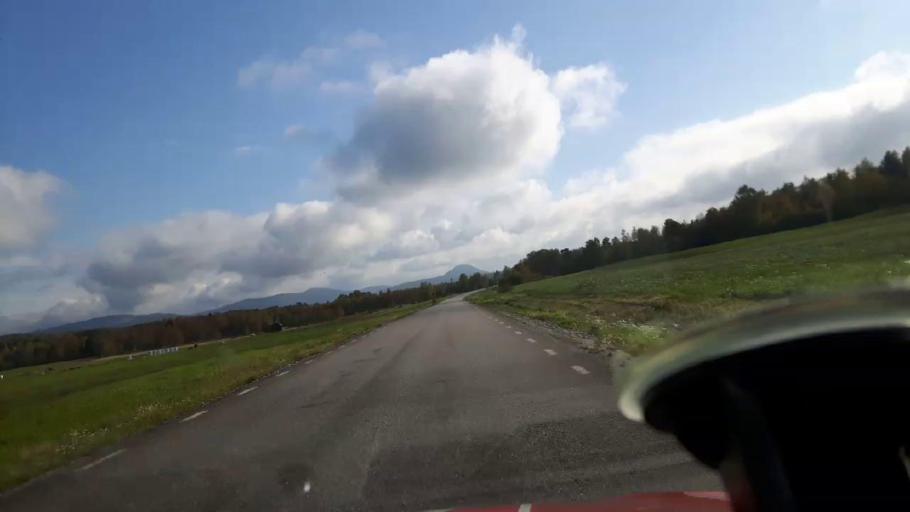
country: SE
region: Gaevleborg
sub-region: Ljusdals Kommun
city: Ljusdal
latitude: 61.7607
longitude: 16.0877
